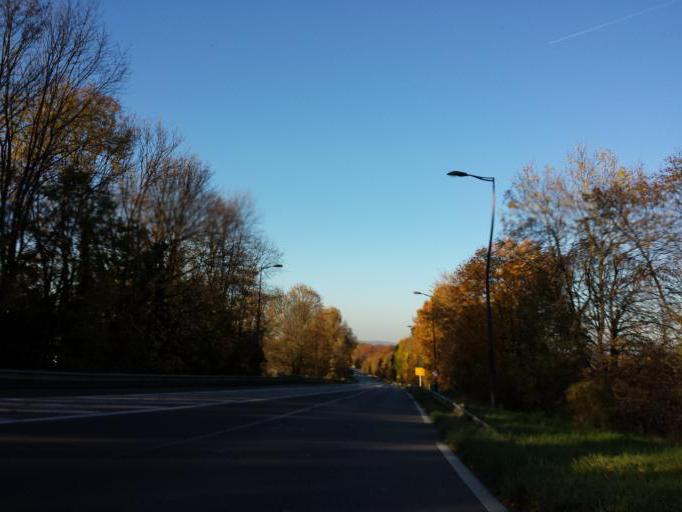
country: FR
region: Ile-de-France
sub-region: Departement du Val-d'Oise
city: Ecouen
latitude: 49.0165
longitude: 2.3860
